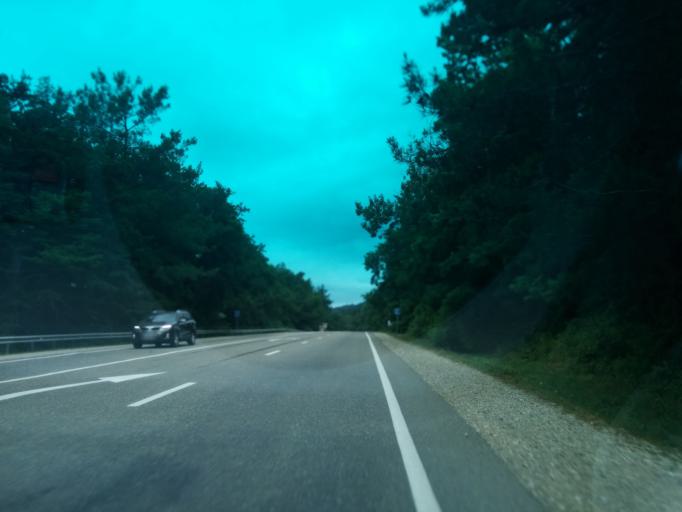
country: RU
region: Krasnodarskiy
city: Ol'ginka
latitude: 44.1803
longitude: 38.9370
